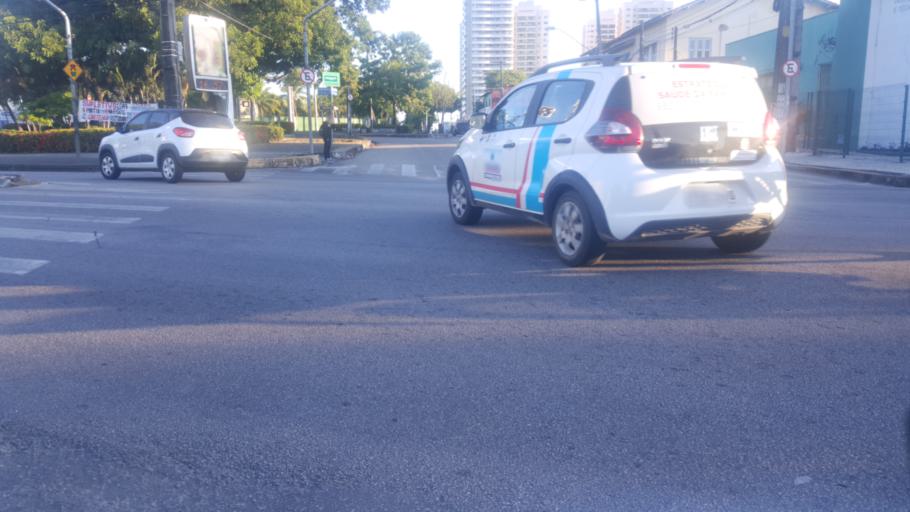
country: BR
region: Ceara
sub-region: Fortaleza
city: Fortaleza
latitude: -3.7443
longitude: -38.5348
